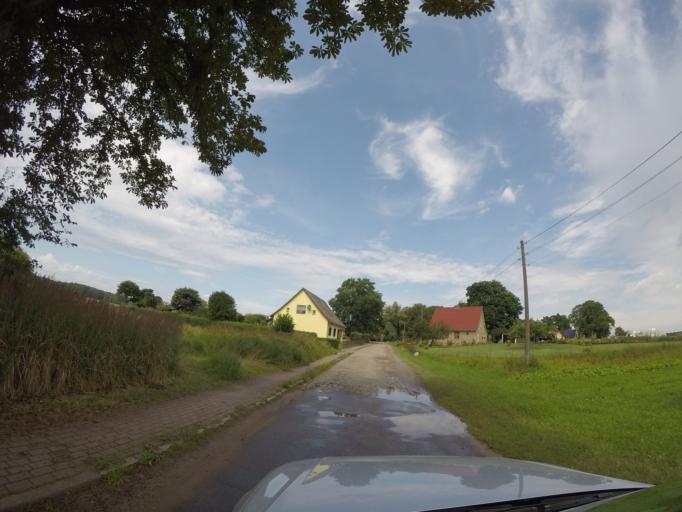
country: DE
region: Mecklenburg-Vorpommern
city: Rechlin
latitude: 53.3389
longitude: 12.8439
